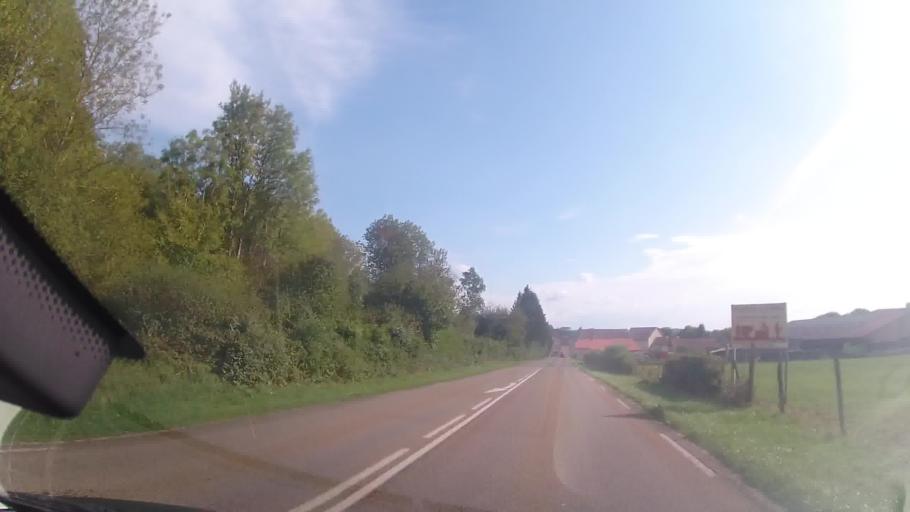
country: FR
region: Franche-Comte
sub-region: Departement du Jura
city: Clairvaux-les-Lacs
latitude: 46.5850
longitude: 5.7593
